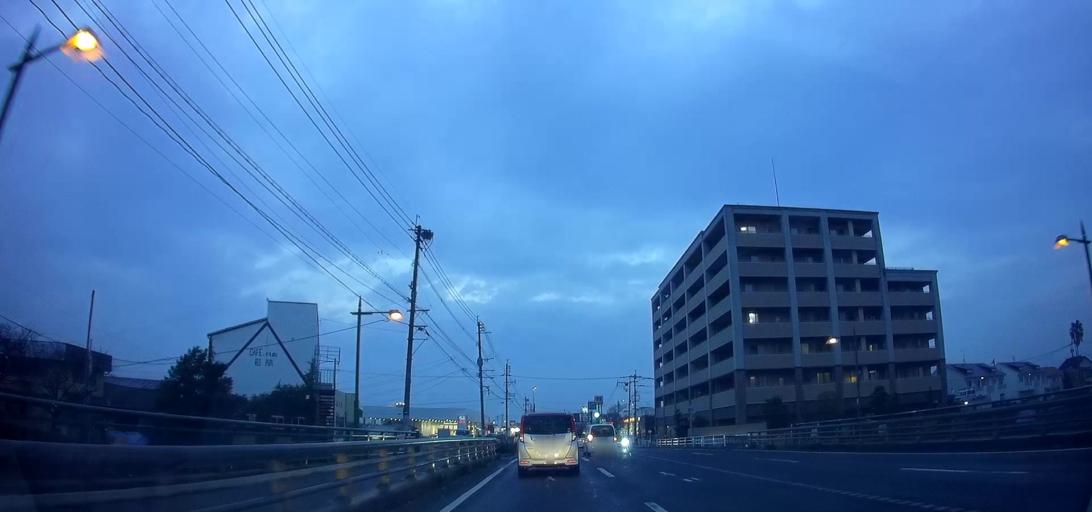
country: JP
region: Nagasaki
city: Omura
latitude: 32.9094
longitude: 129.9540
